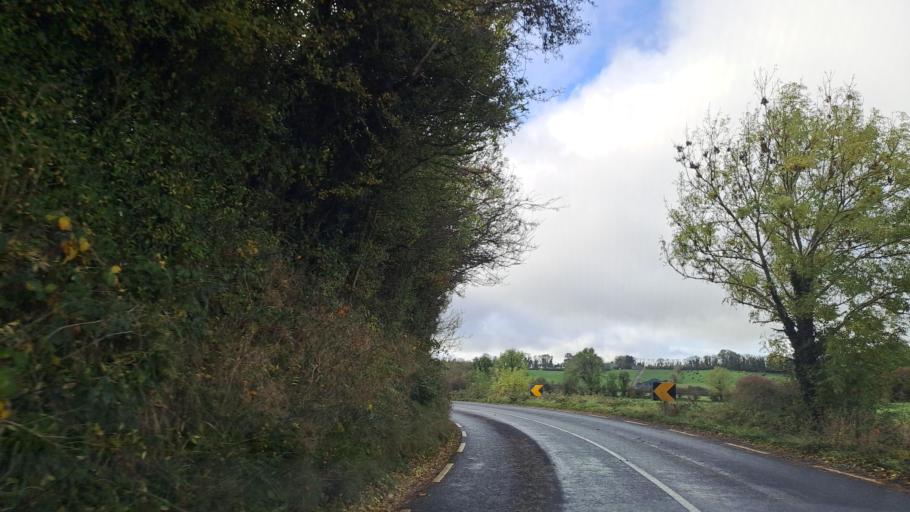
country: IE
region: Ulster
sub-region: An Cabhan
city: Virginia
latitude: 53.8684
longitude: -7.0402
